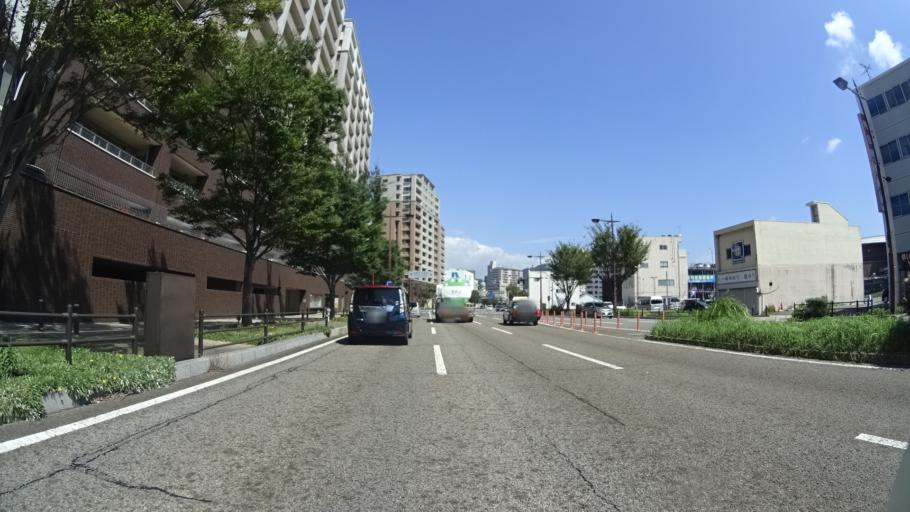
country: JP
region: Yamaguchi
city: Shimonoseki
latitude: 33.9544
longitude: 130.9403
